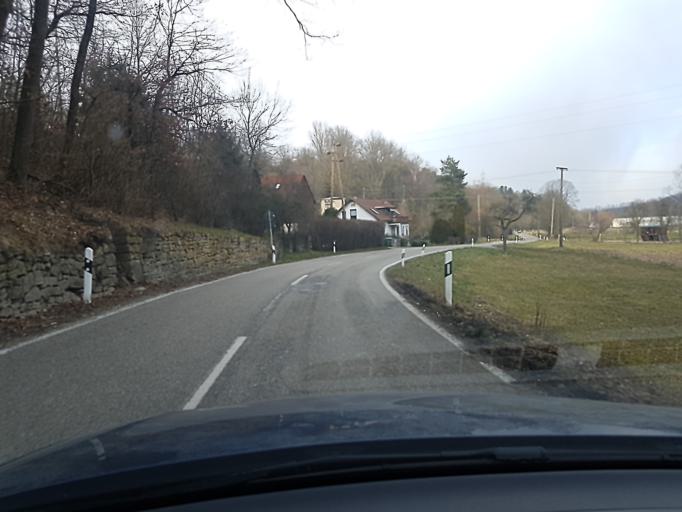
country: DE
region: Baden-Wuerttemberg
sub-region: Regierungsbezirk Stuttgart
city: Eberdingen
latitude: 48.8892
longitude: 8.9615
